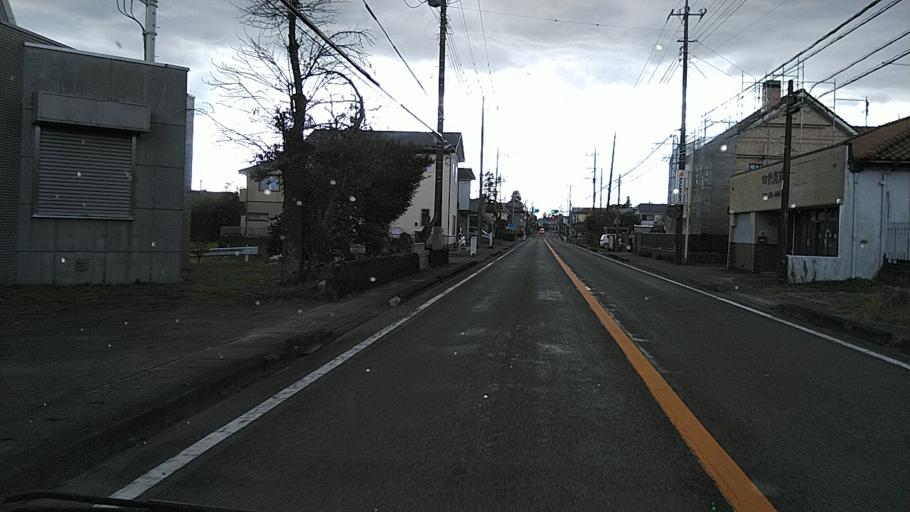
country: JP
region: Shizuoka
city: Gotemba
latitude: 35.3338
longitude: 138.9444
